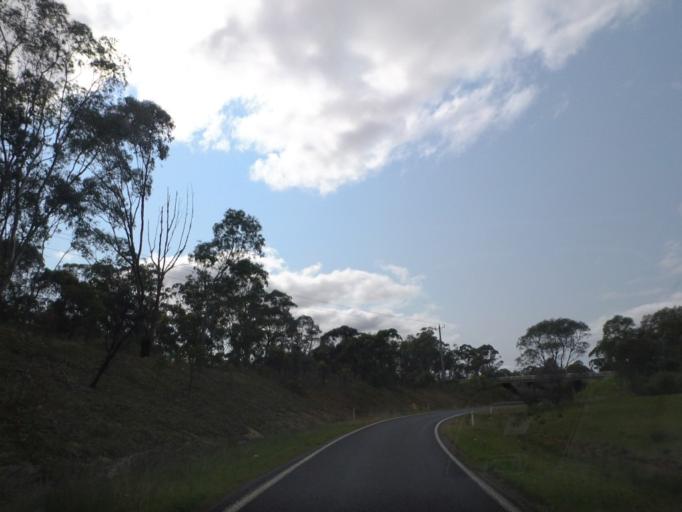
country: AU
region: Victoria
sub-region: Murrindindi
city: Kinglake West
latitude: -37.1082
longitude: 145.0904
